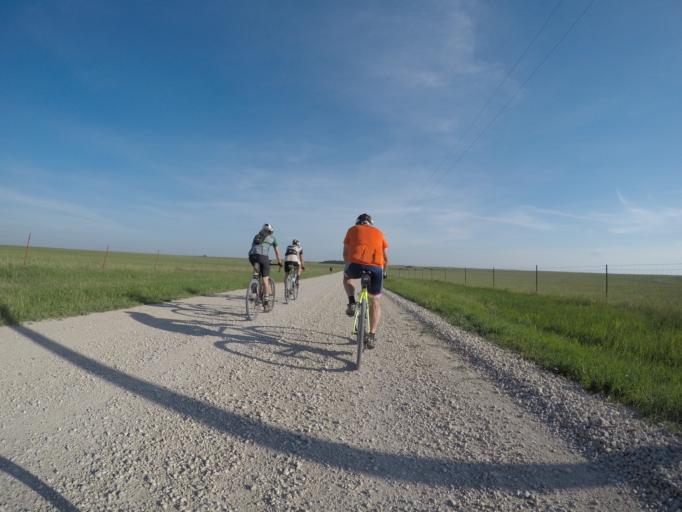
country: US
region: Kansas
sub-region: Riley County
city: Manhattan
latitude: 39.0281
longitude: -96.4918
